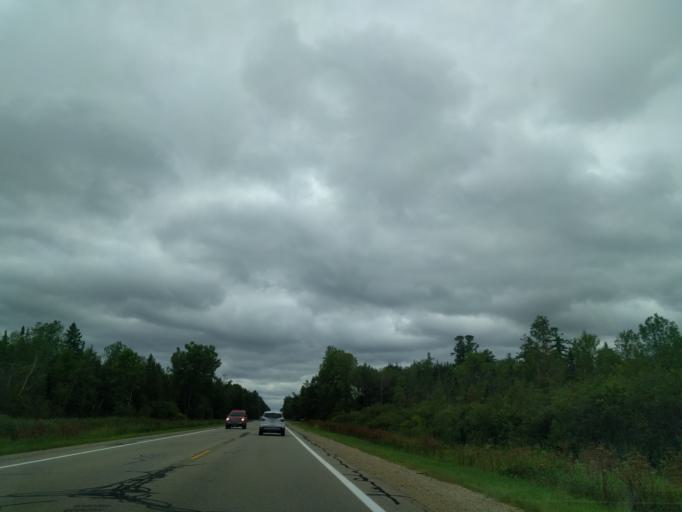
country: US
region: Michigan
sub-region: Menominee County
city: Menominee
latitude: 45.3526
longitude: -87.4044
